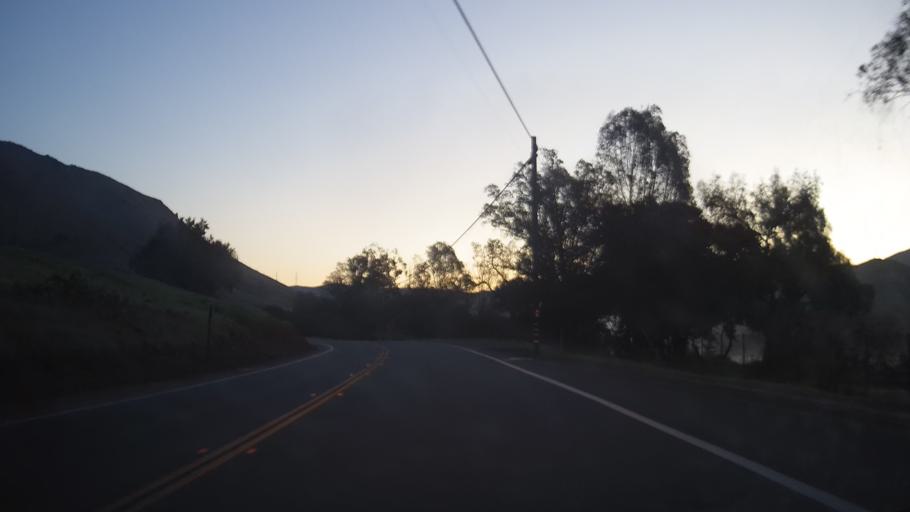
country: US
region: California
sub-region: San Diego County
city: Crest
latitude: 32.7805
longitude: -116.8620
